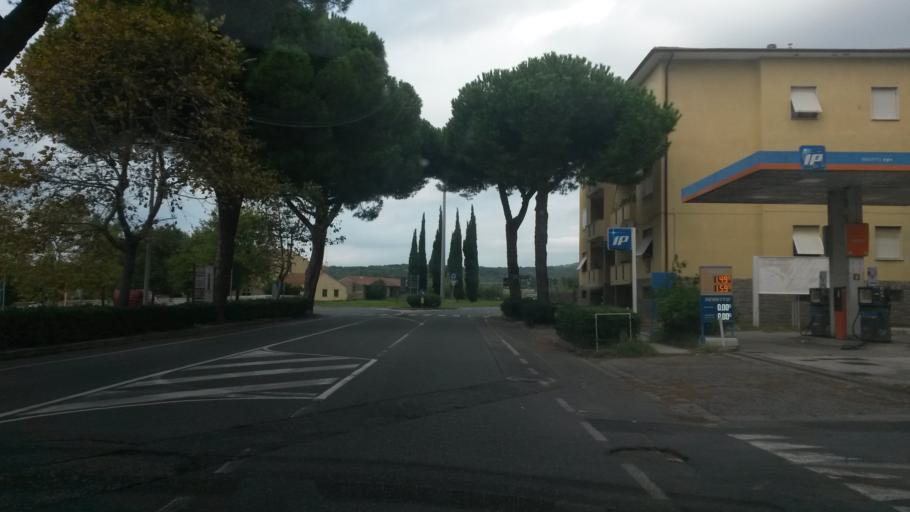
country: IT
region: Tuscany
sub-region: Provincia di Livorno
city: Rosignano Solvay-Castiglioncello
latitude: 43.3966
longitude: 10.4358
